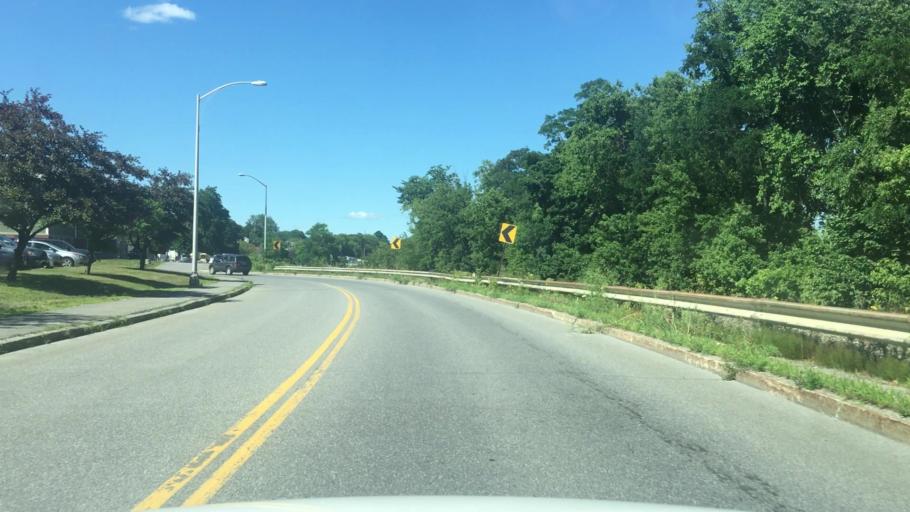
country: US
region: Maine
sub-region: Kennebec County
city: Waterville
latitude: 44.5580
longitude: -69.6267
